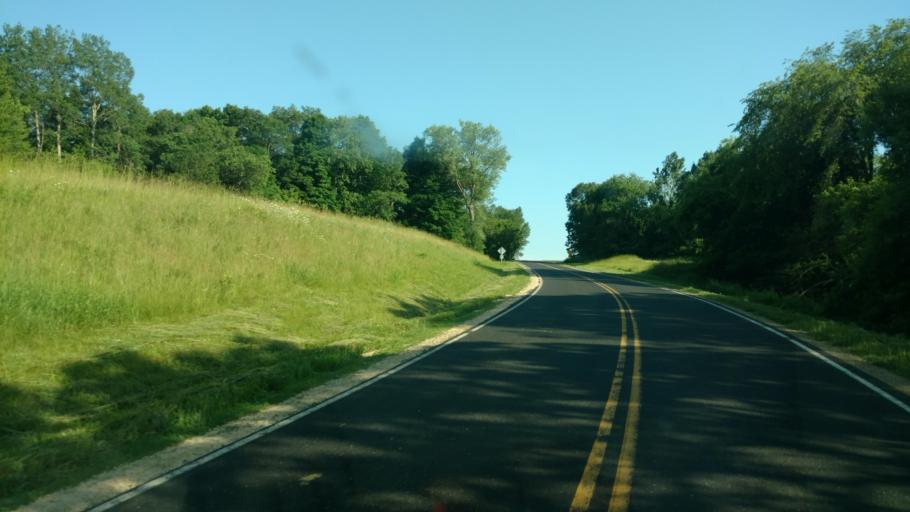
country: US
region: Wisconsin
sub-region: Vernon County
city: Hillsboro
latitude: 43.6851
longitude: -90.3451
